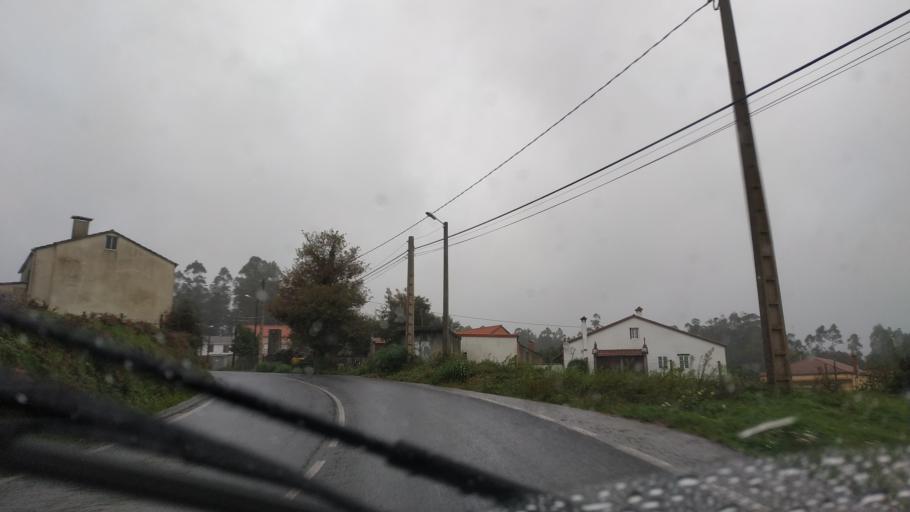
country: ES
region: Galicia
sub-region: Provincia da Coruna
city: Negreira
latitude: 42.9111
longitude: -8.7647
